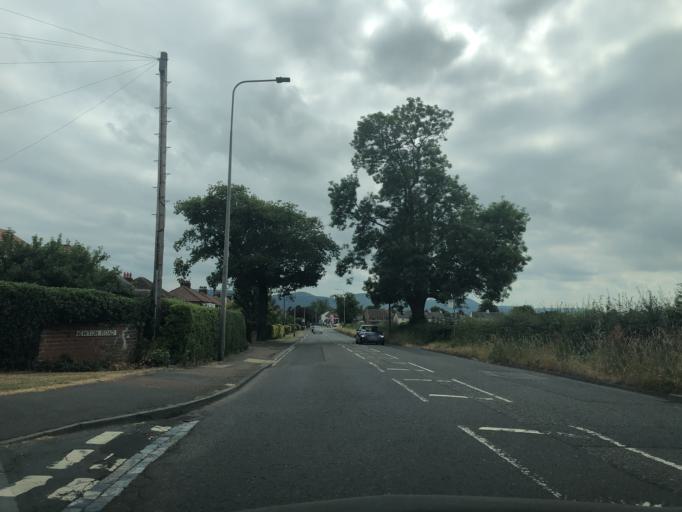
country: GB
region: England
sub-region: North Yorkshire
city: Great Ayton
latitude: 54.4979
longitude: -1.1310
